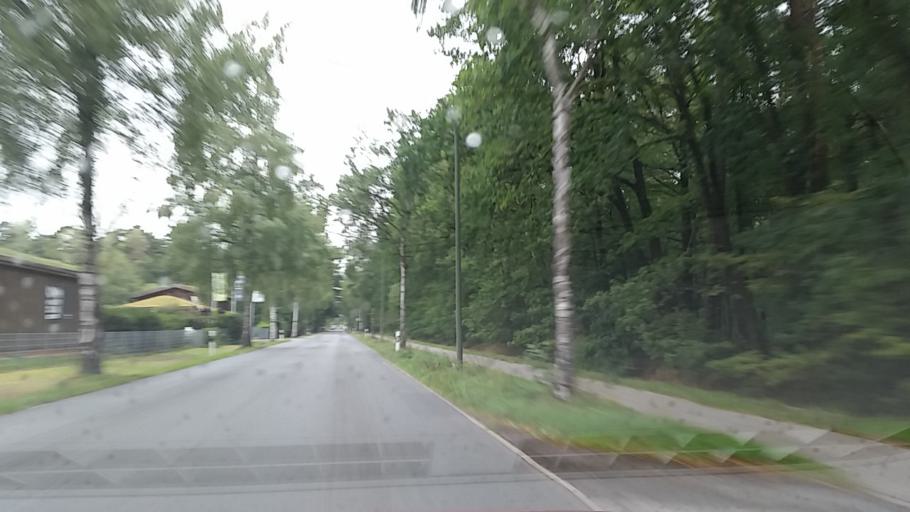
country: DE
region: North Rhine-Westphalia
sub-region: Regierungsbezirk Munster
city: Lotte
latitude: 52.2754
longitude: 7.9549
